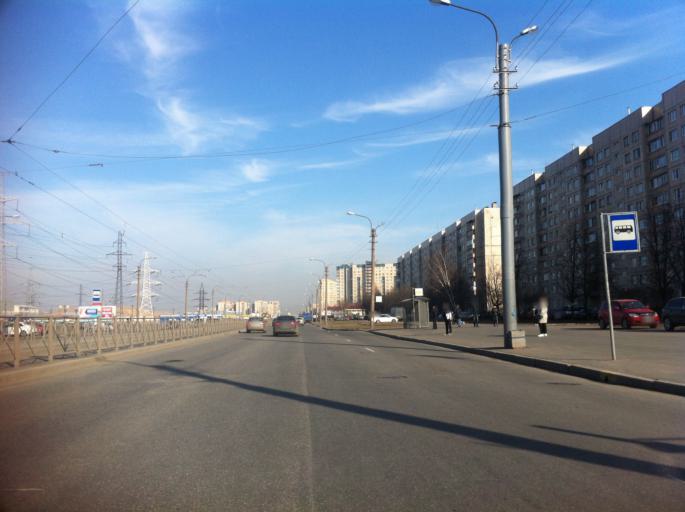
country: RU
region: St.-Petersburg
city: Uritsk
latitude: 59.8600
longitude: 30.2067
